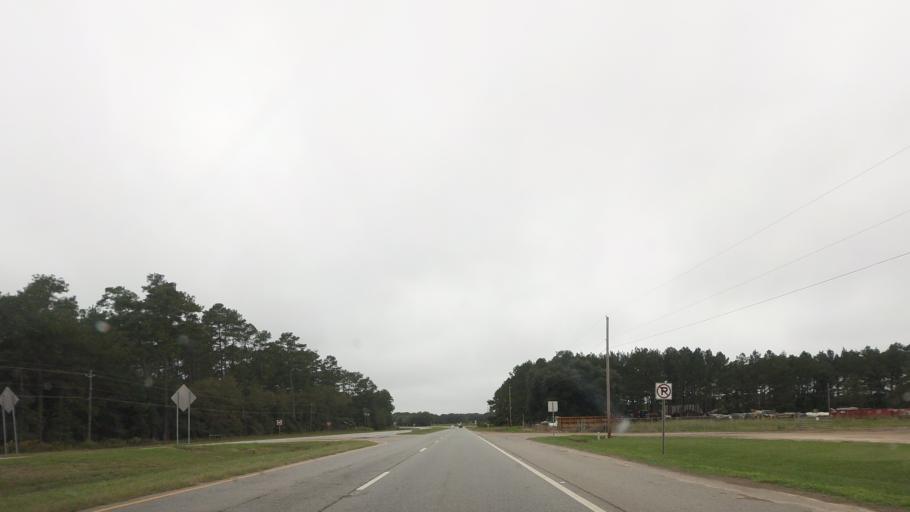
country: US
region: Georgia
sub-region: Berrien County
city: Enigma
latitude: 31.3933
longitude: -83.2346
